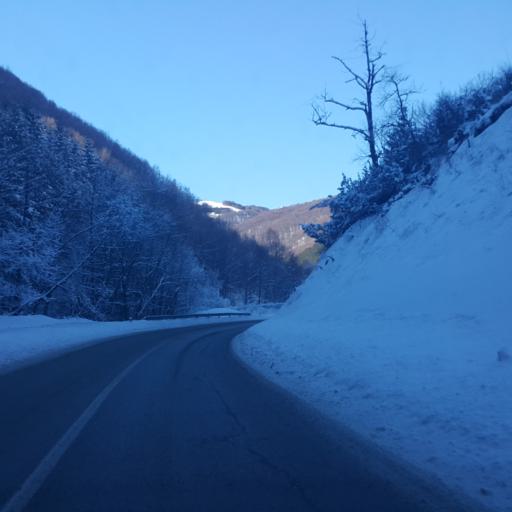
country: XK
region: Mitrovica
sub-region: Komuna e Leposaviqit
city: Leposaviq
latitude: 43.3023
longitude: 20.8941
